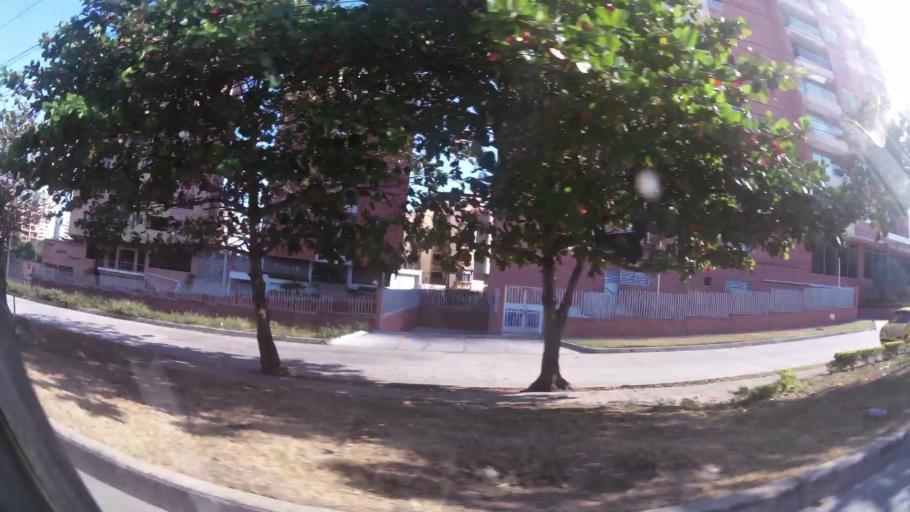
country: CO
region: Atlantico
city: Barranquilla
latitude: 11.0089
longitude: -74.8352
